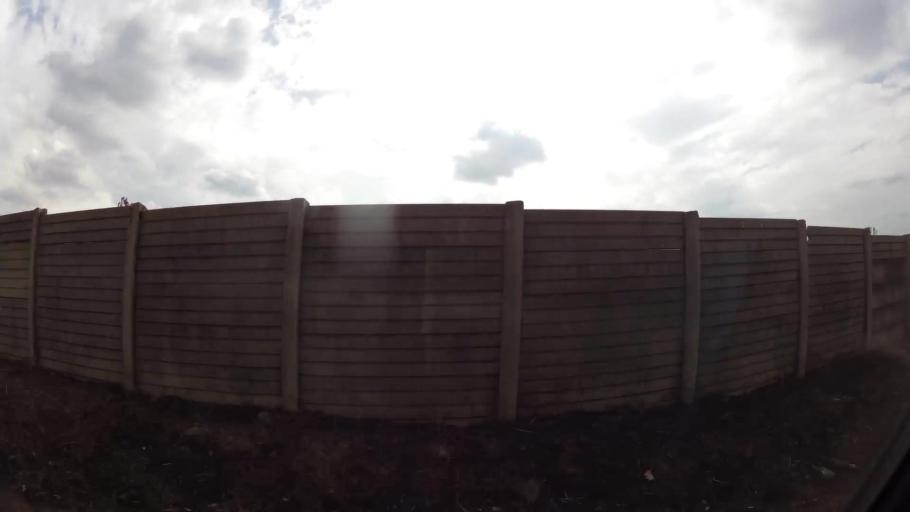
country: ZA
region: Gauteng
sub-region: City of Johannesburg Metropolitan Municipality
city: Roodepoort
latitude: -26.1008
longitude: 27.8850
